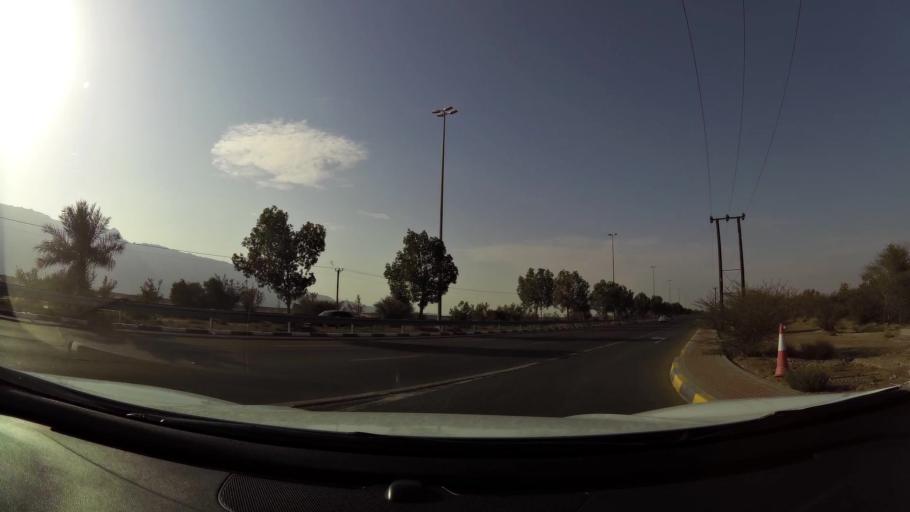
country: AE
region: Abu Dhabi
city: Al Ain
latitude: 24.0595
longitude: 55.8389
